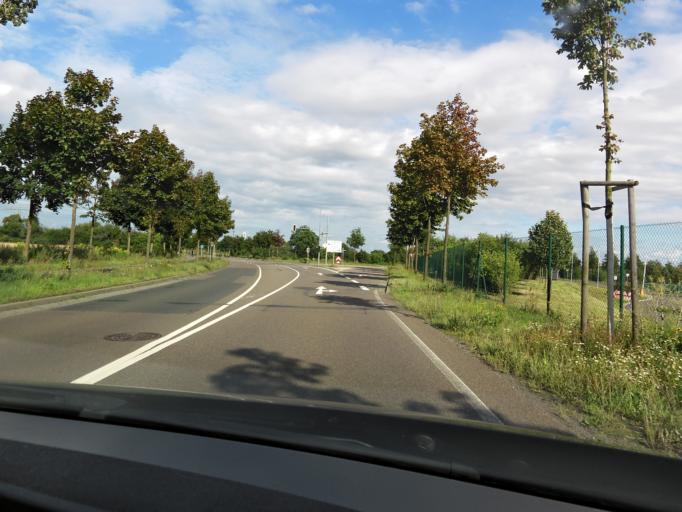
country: DE
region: Saxony
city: Taucha
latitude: 51.3957
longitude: 12.4360
